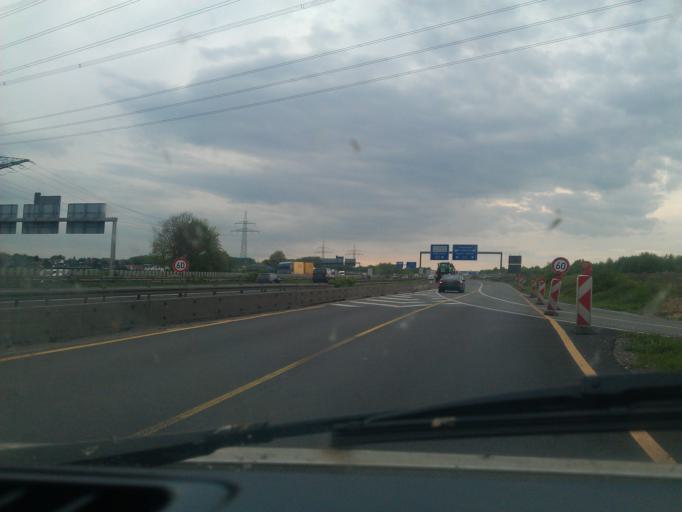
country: DE
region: North Rhine-Westphalia
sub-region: Regierungsbezirk Koln
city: Wurselen
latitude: 50.8049
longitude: 6.1677
